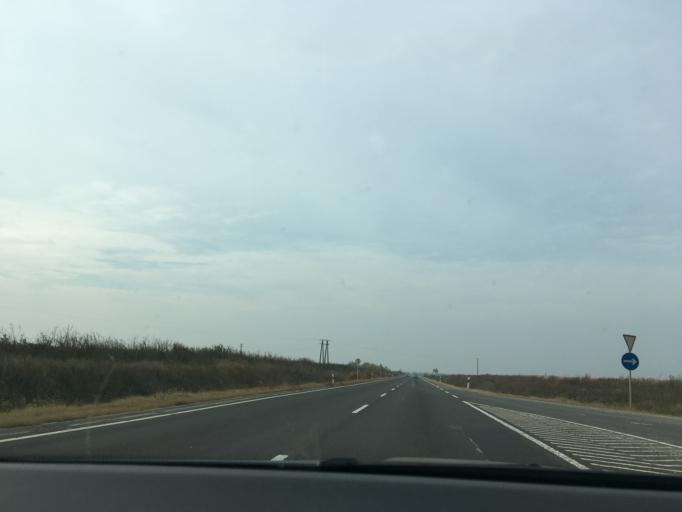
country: HU
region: Jasz-Nagykun-Szolnok
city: Torokszentmiklos
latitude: 47.1933
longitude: 20.4427
